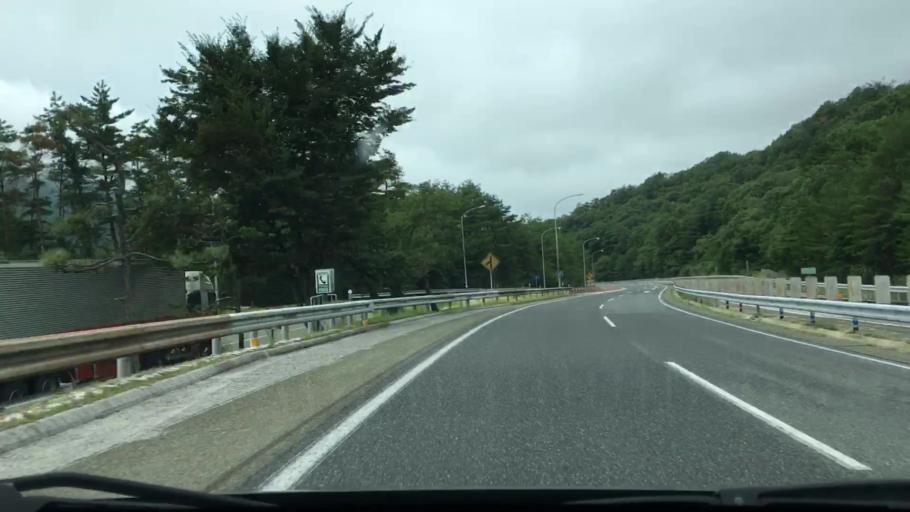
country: JP
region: Hiroshima
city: Shobara
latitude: 34.8621
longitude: 133.1039
